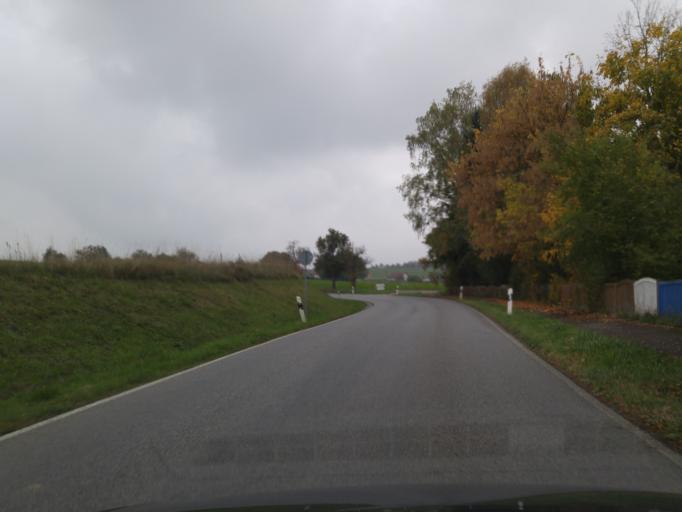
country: DE
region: Baden-Wuerttemberg
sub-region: Regierungsbezirk Stuttgart
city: Bad Rappenau
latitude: 49.2097
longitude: 9.0925
